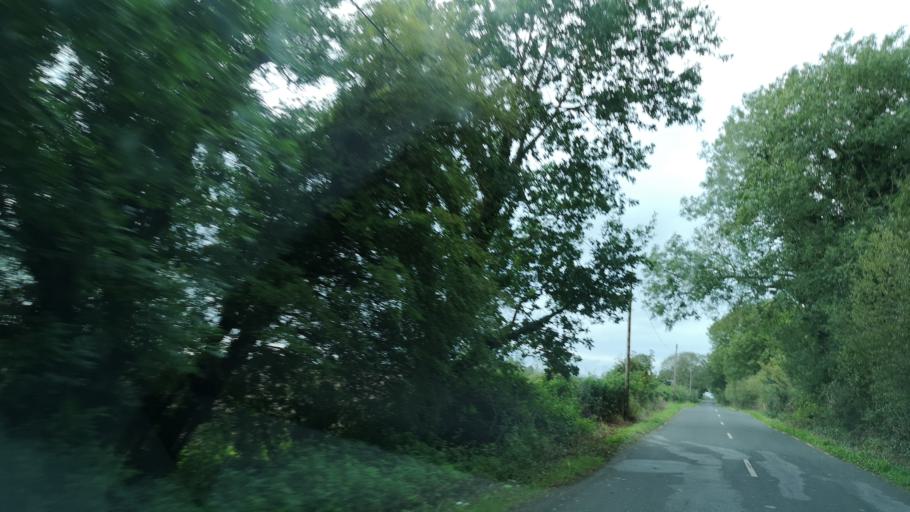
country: IE
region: Leinster
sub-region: Uibh Fhaili
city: Ferbane
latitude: 53.1996
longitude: -7.7812
